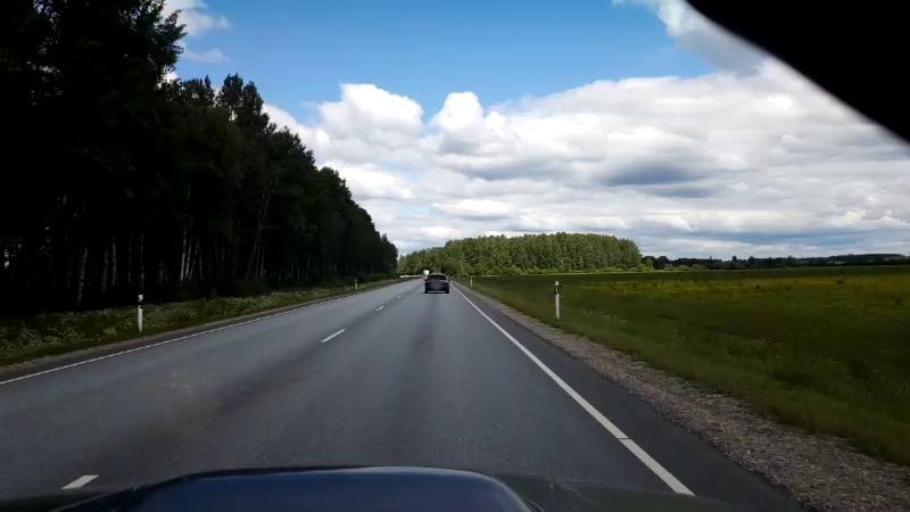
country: EE
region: Paernumaa
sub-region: Sauga vald
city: Sauga
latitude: 58.4705
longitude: 24.5244
